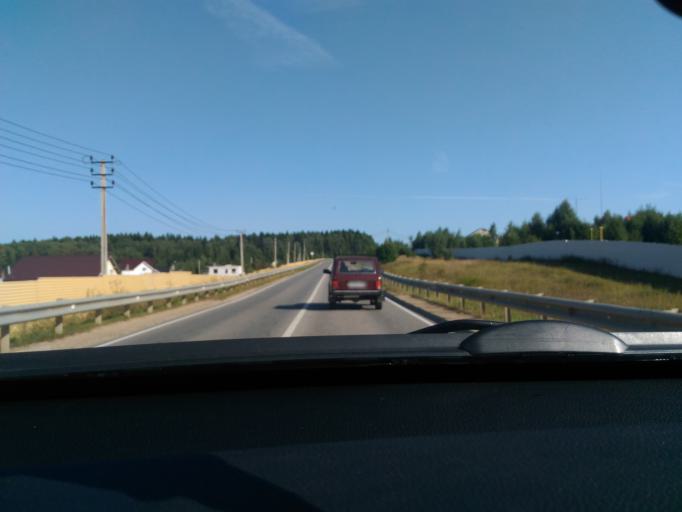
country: RU
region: Moskovskaya
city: Dedenevo
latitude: 56.2434
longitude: 37.5472
